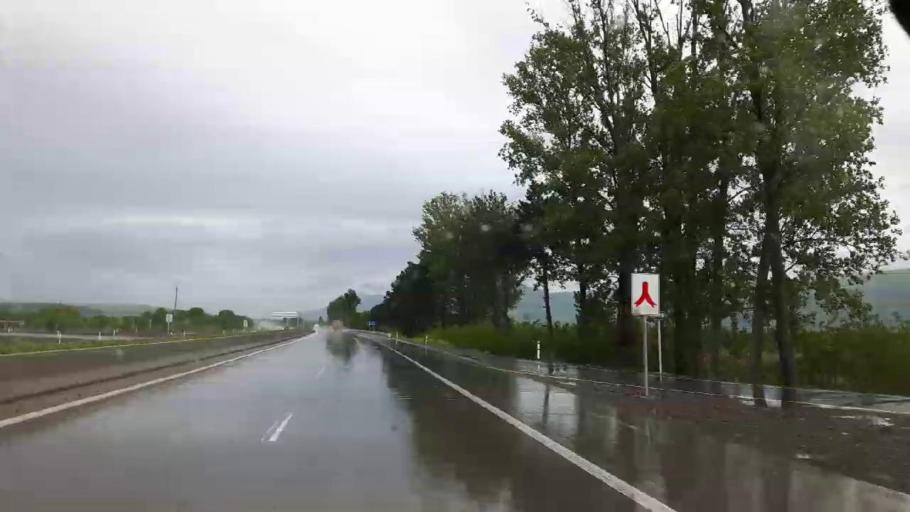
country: GE
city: Agara
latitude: 42.0313
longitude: 43.9505
